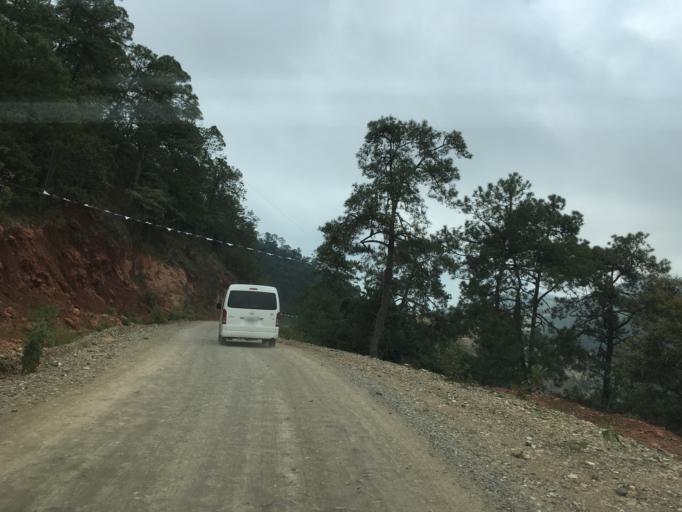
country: MX
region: Oaxaca
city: Santiago Tilantongo
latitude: 17.2034
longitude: -97.2806
